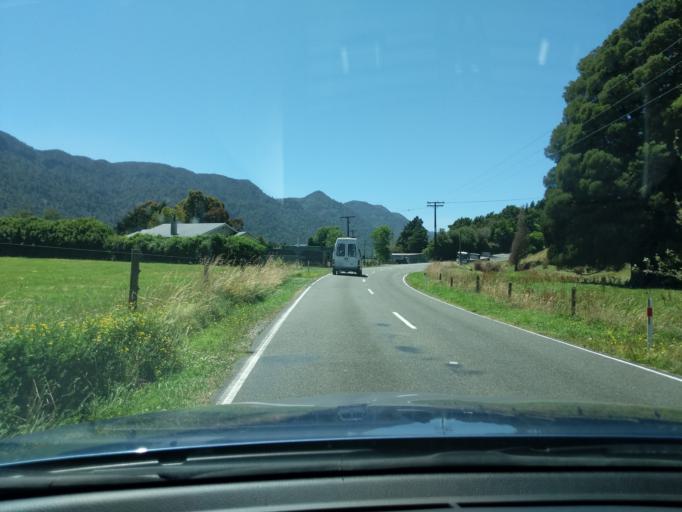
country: NZ
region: Tasman
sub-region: Tasman District
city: Takaka
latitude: -40.6970
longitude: 172.6327
